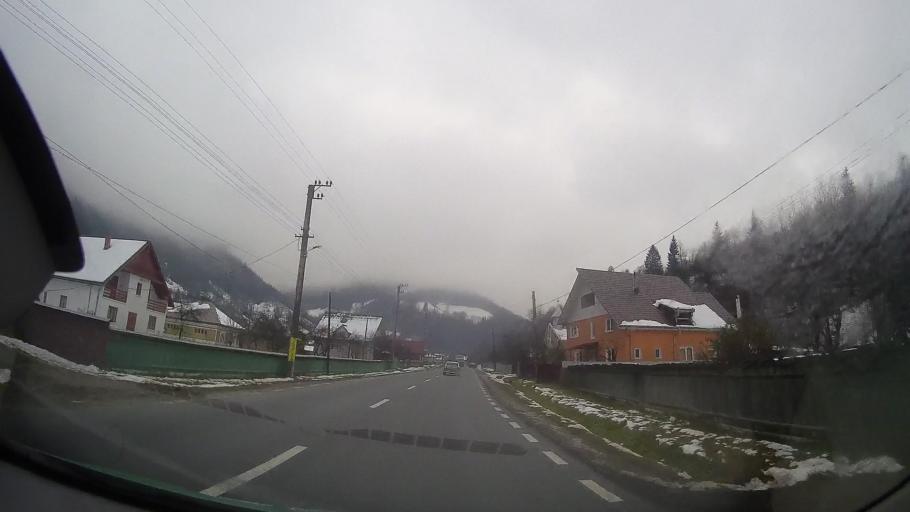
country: RO
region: Neamt
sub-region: Comuna Bicazu Ardelean
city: Bicazu Ardelean
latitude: 46.8576
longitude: 25.9364
